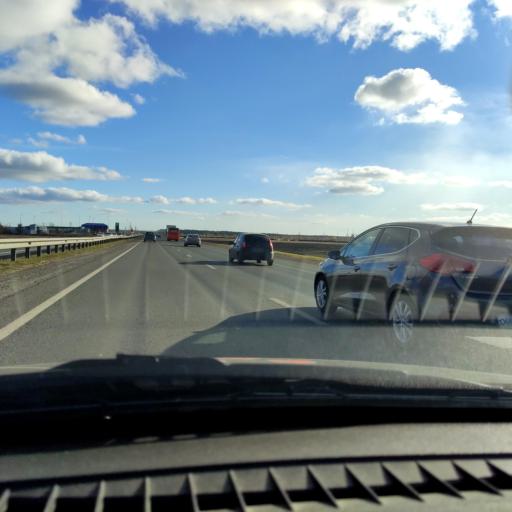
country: RU
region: Samara
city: Tol'yatti
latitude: 53.5599
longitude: 49.4995
